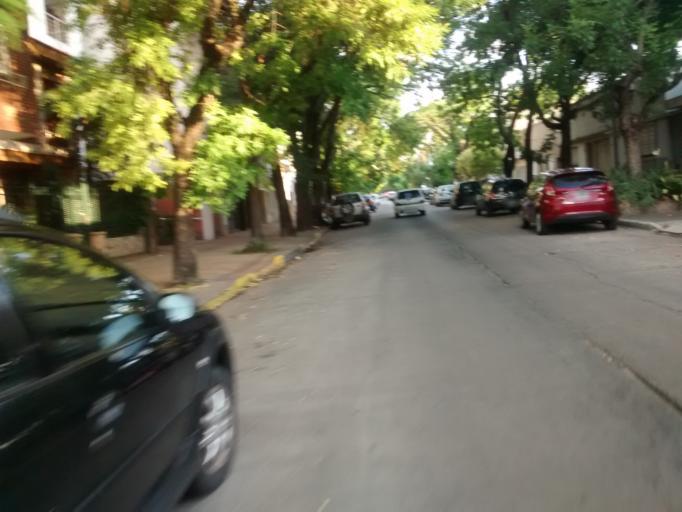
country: AR
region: Buenos Aires
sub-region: Partido de La Plata
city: La Plata
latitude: -34.9124
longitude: -57.9691
